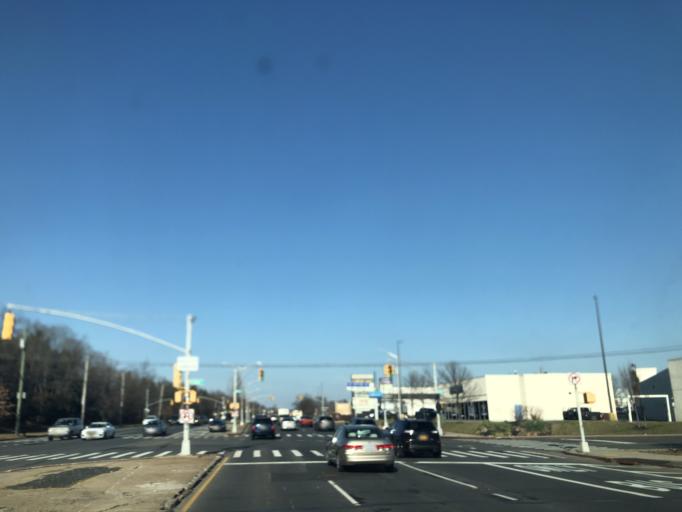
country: US
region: New York
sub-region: Richmond County
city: Staten Island
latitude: 40.5763
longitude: -74.1698
